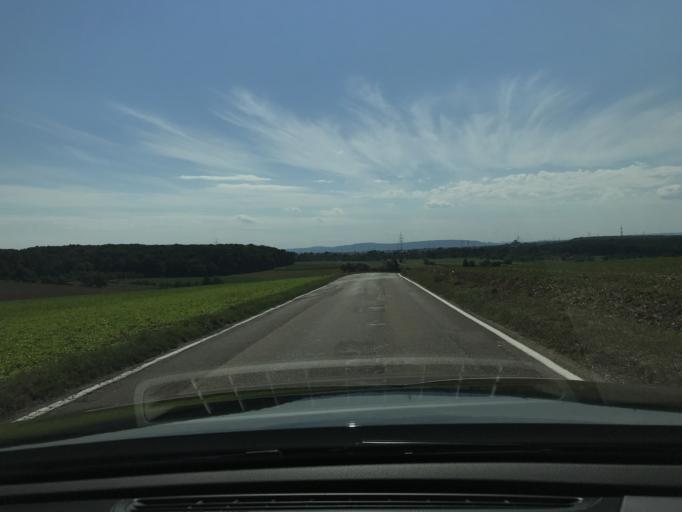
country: DE
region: Baden-Wuerttemberg
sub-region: Regierungsbezirk Stuttgart
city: Affalterbach
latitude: 48.9118
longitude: 9.3151
